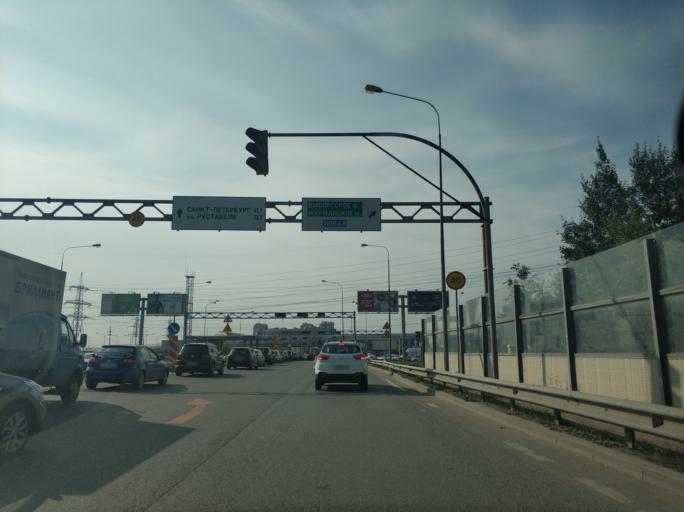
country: RU
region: Leningrad
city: Murino
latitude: 60.0425
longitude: 30.4439
